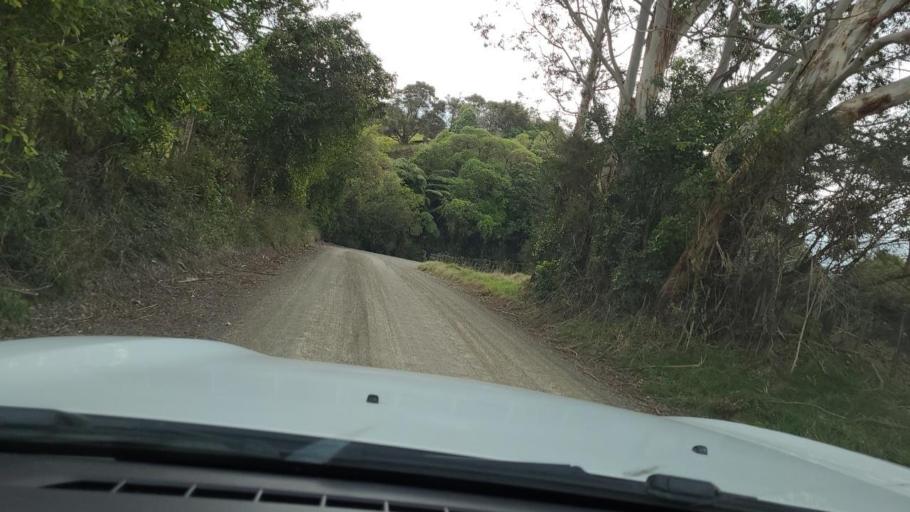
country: NZ
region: Hawke's Bay
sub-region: Napier City
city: Napier
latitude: -39.2854
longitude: 176.8433
